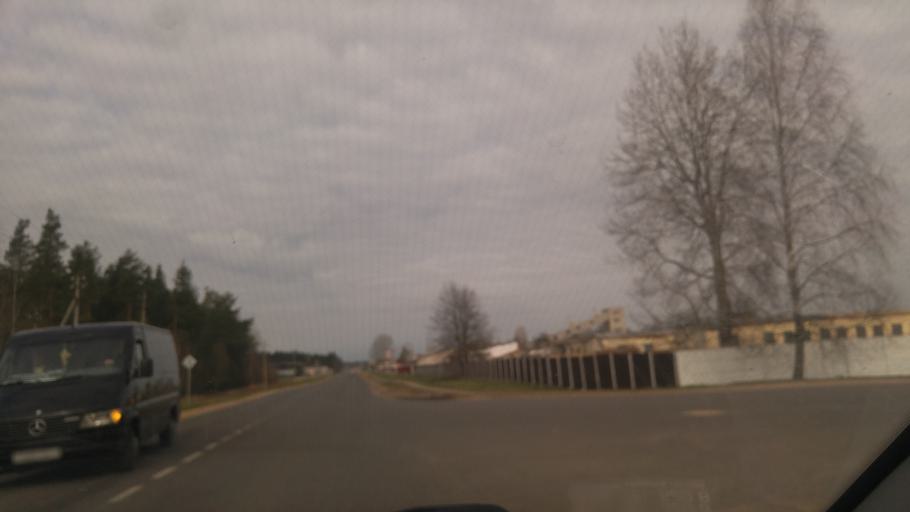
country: BY
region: Minsk
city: Chervyen'
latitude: 53.6961
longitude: 28.4301
